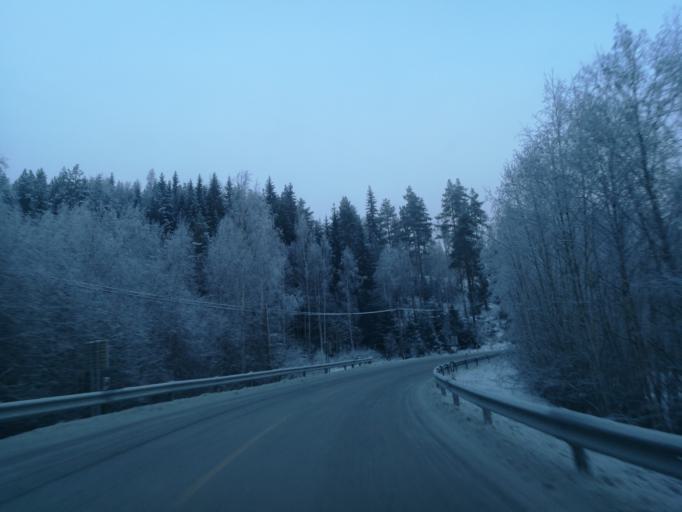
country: NO
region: Hedmark
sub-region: Kongsvinger
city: Kongsvinger
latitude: 60.2818
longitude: 12.1514
